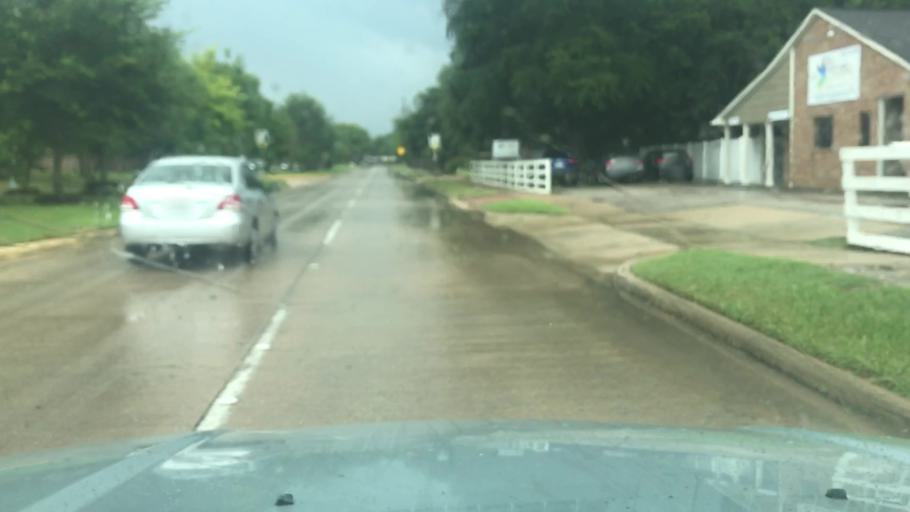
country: US
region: Texas
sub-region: Fort Bend County
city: Cinco Ranch
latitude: 29.7424
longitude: -95.7894
